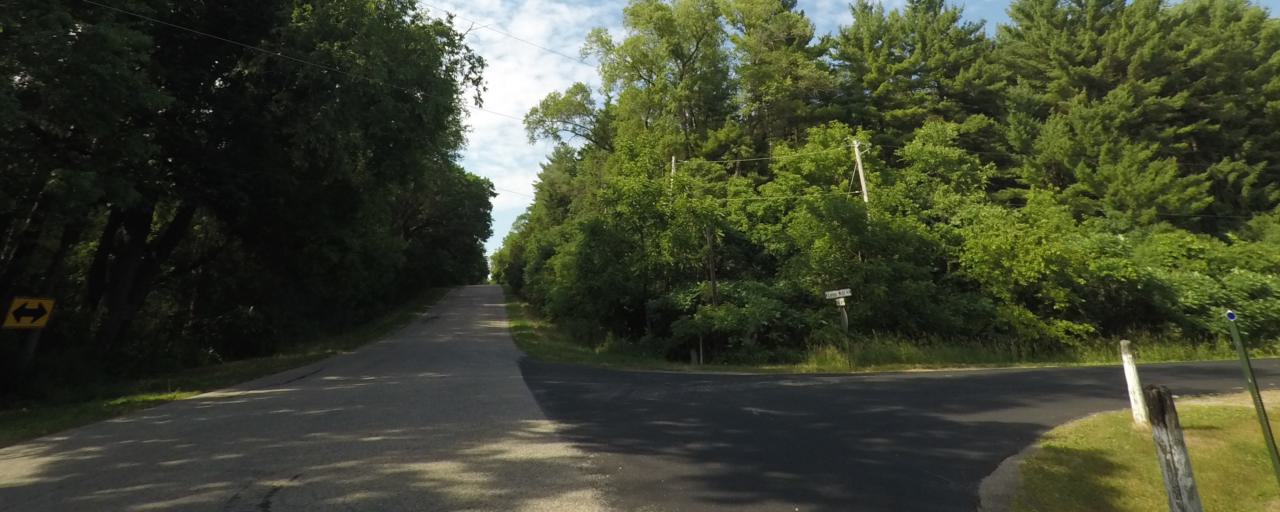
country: US
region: Wisconsin
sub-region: Walworth County
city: Elkhorn
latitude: 42.7783
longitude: -88.5439
